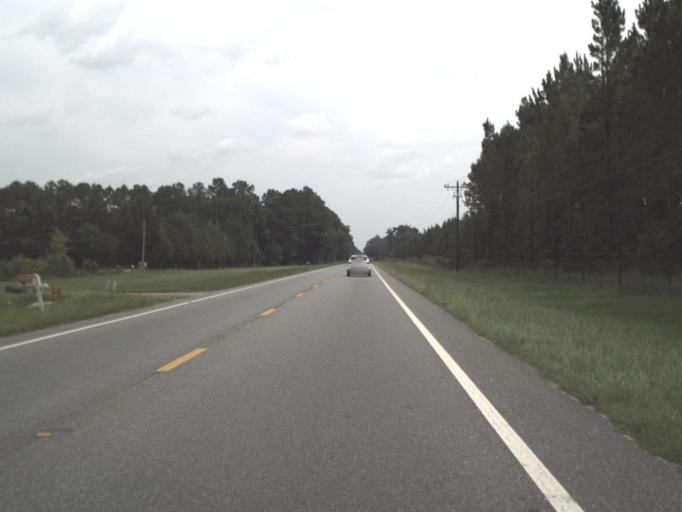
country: US
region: Florida
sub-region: Columbia County
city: Watertown
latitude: 30.0558
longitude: -82.5992
